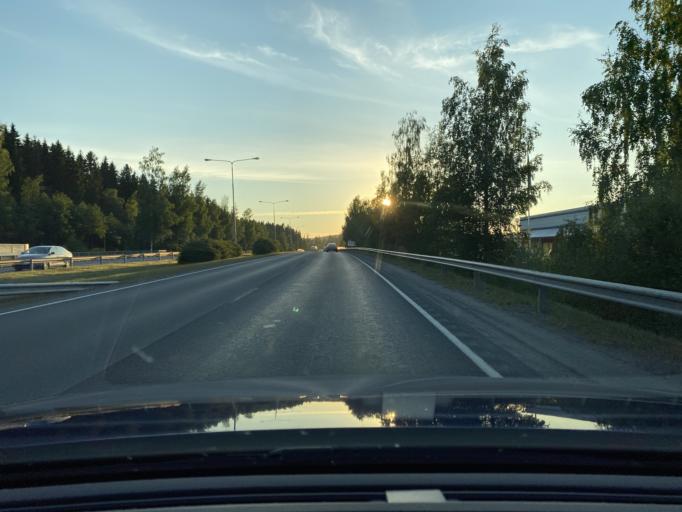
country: FI
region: Pirkanmaa
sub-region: Tampere
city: Pirkkala
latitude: 61.5160
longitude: 23.6594
